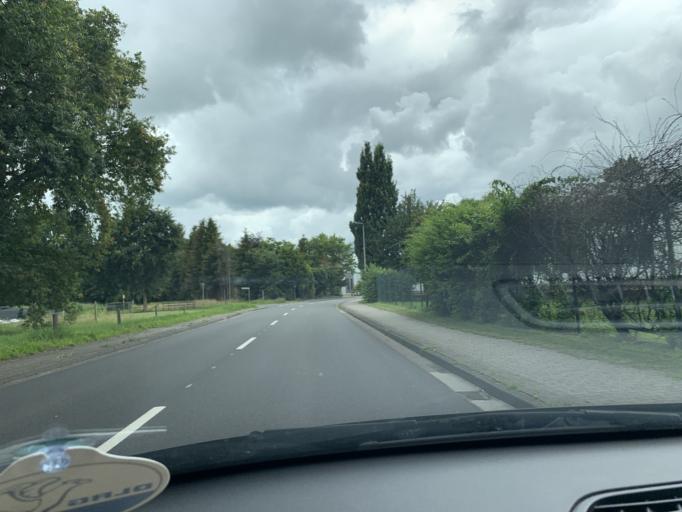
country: DE
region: Lower Saxony
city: Edewecht
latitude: 53.1129
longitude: 7.9747
